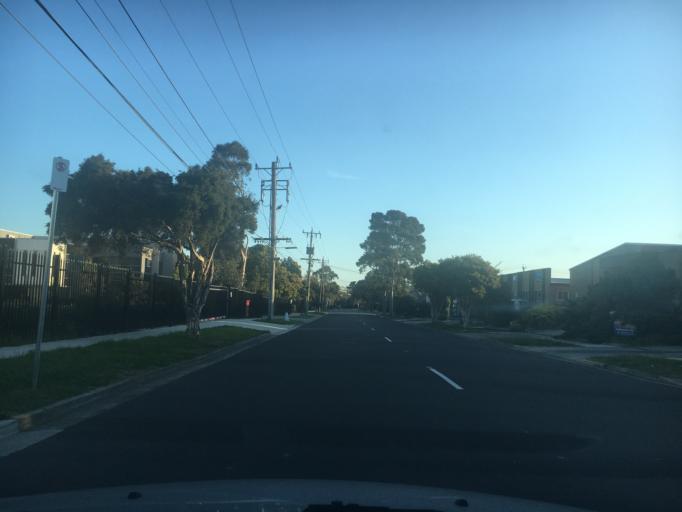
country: AU
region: Victoria
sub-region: Monash
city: Clayton
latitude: -37.9219
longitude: 145.1353
